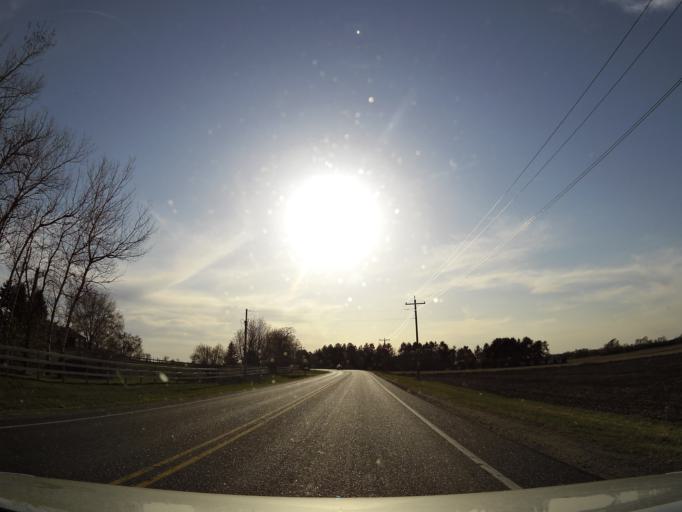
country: US
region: Wisconsin
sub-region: Pierce County
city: River Falls
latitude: 44.8258
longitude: -92.6887
